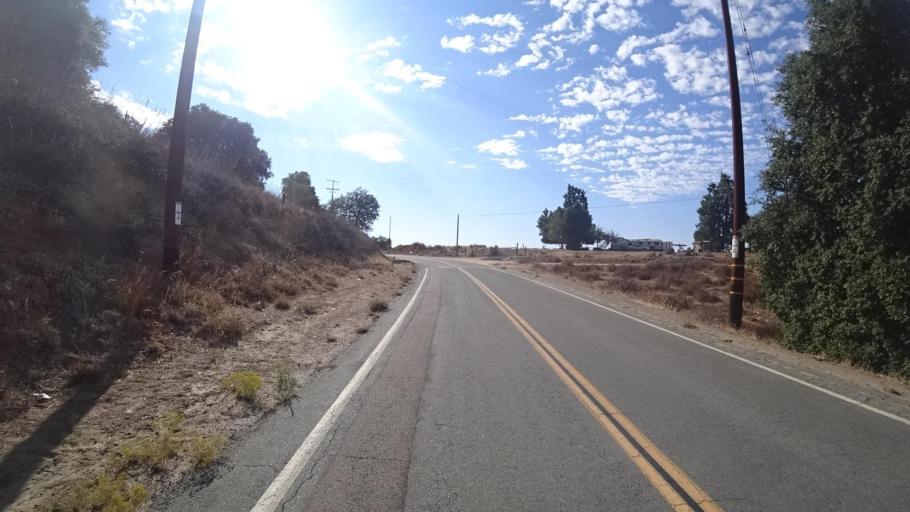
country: US
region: California
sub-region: San Diego County
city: Ramona
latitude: 33.1829
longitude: -116.7748
